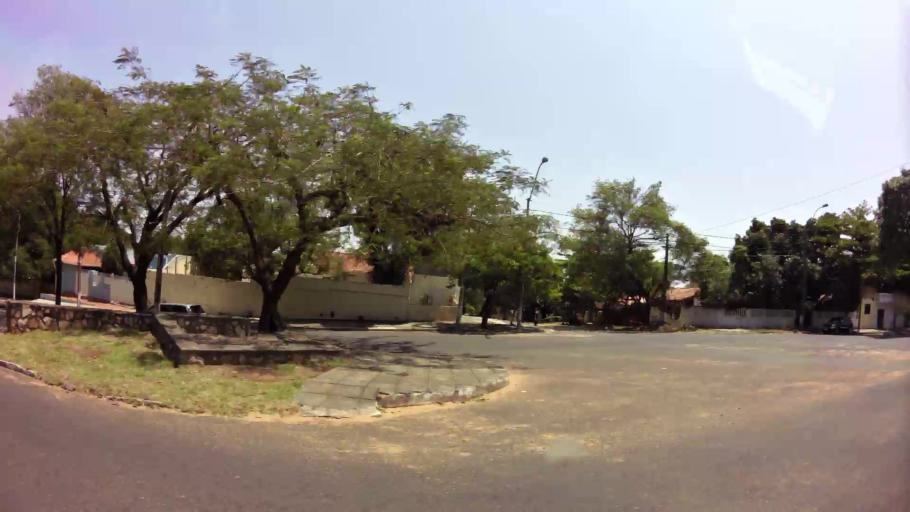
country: PY
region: Asuncion
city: Asuncion
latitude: -25.3052
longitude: -57.6388
